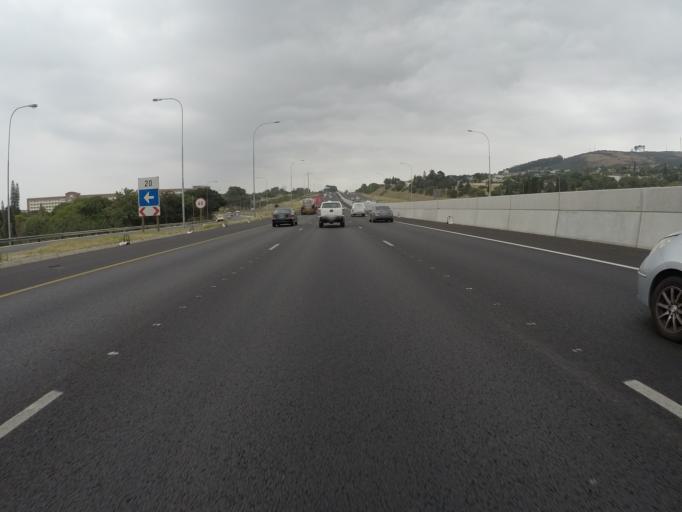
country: ZA
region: Western Cape
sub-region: City of Cape Town
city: Kraaifontein
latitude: -33.8892
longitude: 18.6130
